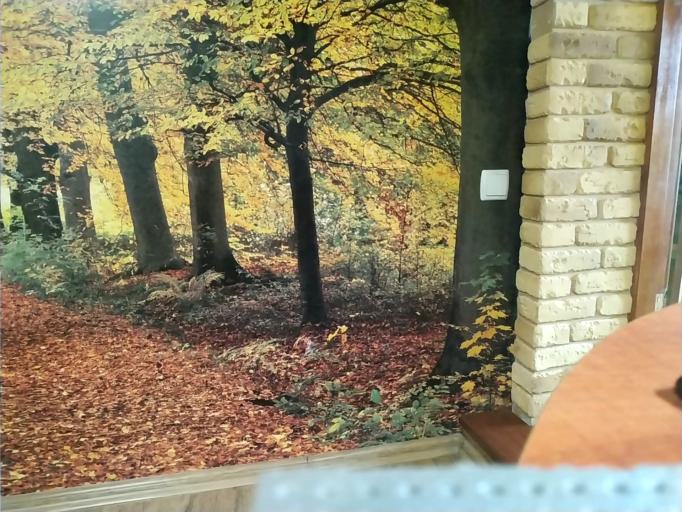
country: RU
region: Tverskaya
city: Staritsa
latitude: 56.5475
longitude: 34.9294
